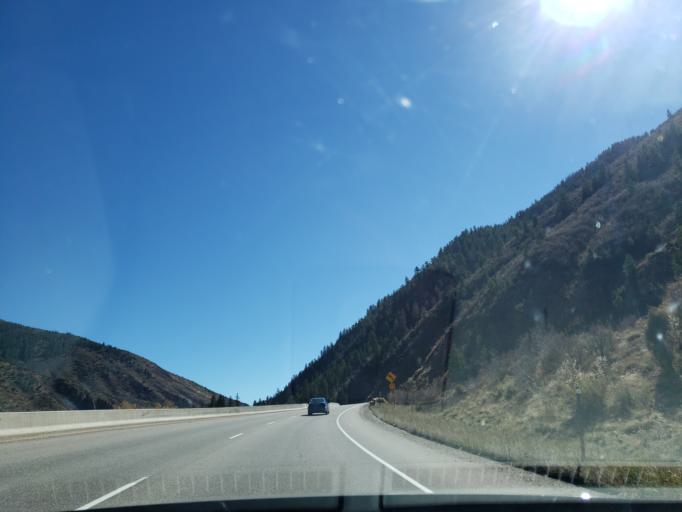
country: US
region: Colorado
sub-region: Eagle County
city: Basalt
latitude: 39.3227
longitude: -106.9470
